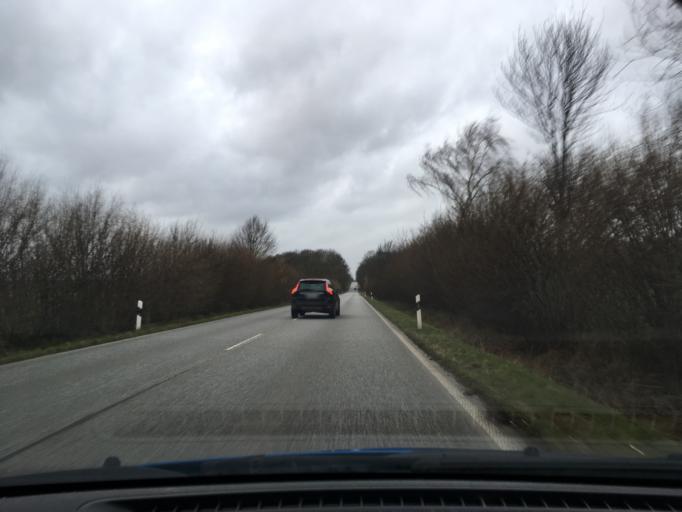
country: DE
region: Schleswig-Holstein
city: Wangelau
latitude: 53.4580
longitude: 10.5484
